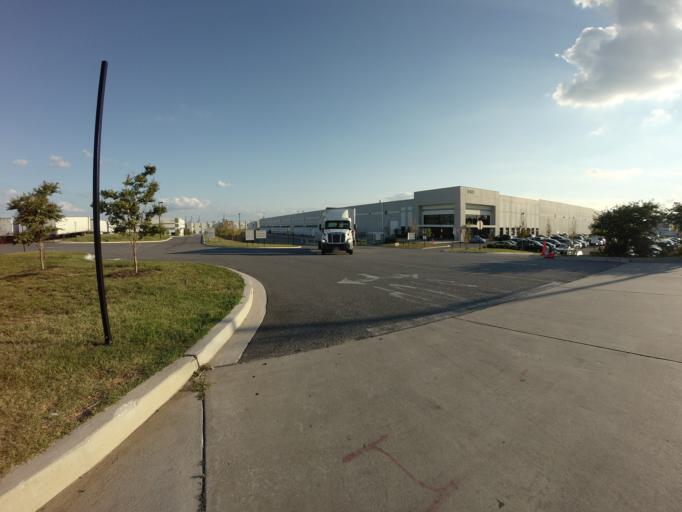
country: US
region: Maryland
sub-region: Baltimore County
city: Dundalk
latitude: 39.2718
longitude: -76.5467
